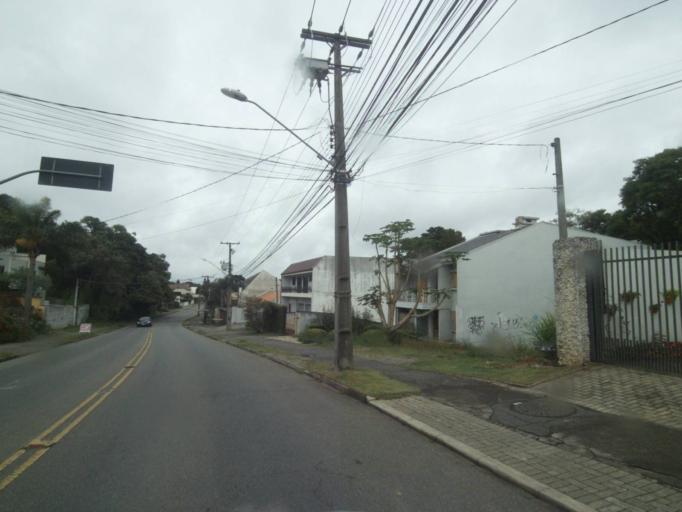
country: BR
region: Parana
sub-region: Curitiba
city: Curitiba
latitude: -25.4206
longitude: -49.3239
